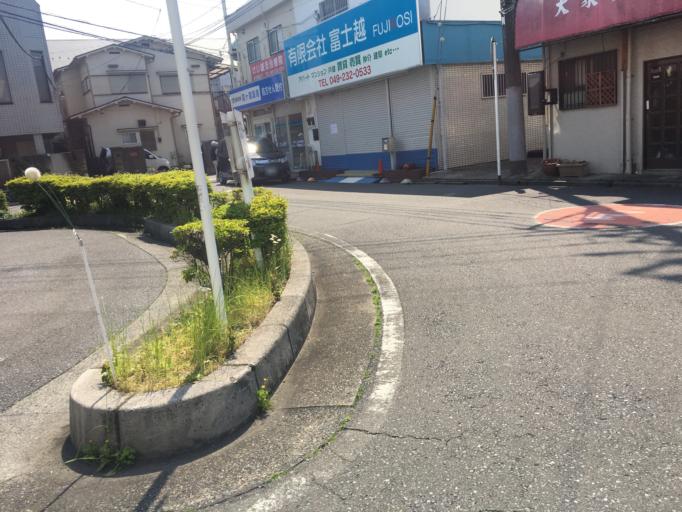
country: JP
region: Saitama
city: Kawagoe
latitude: 35.9253
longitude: 139.4426
